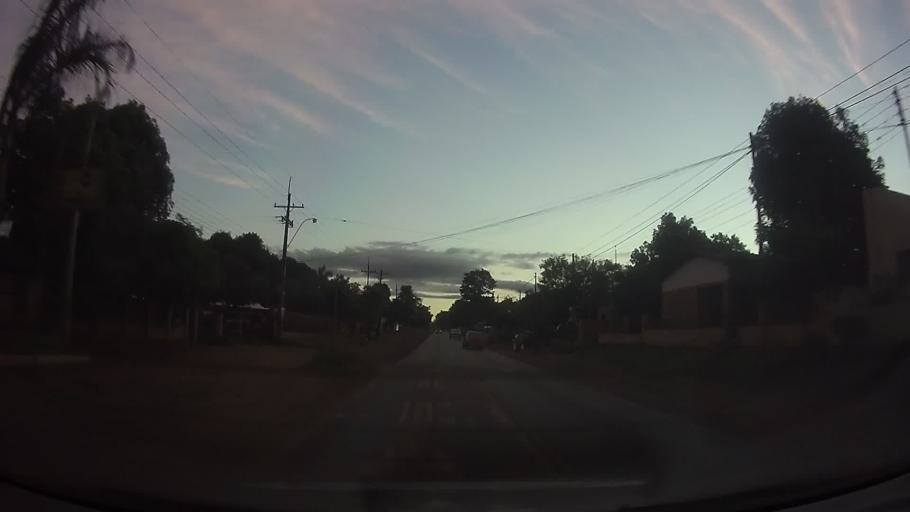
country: PY
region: Central
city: Ita
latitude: -25.4377
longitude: -57.3676
